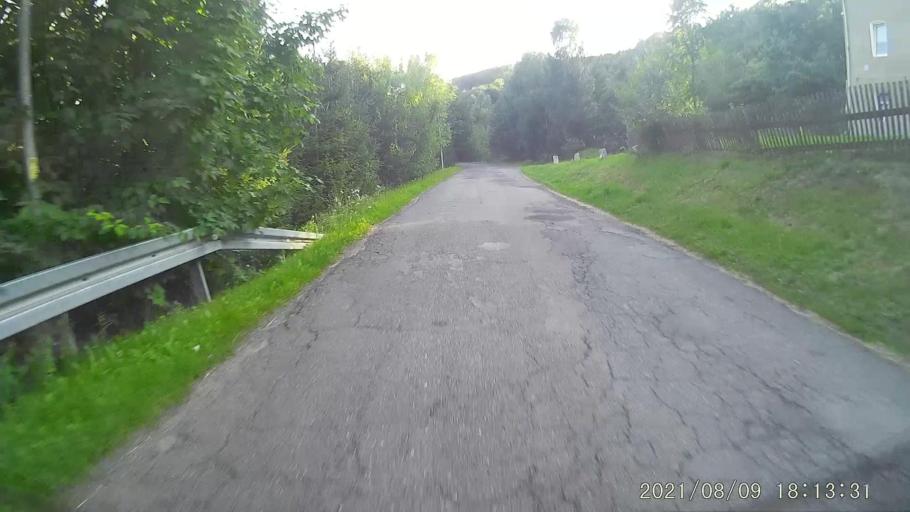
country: PL
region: Lower Silesian Voivodeship
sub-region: Powiat klodzki
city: Klodzko
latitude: 50.4930
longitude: 16.6647
